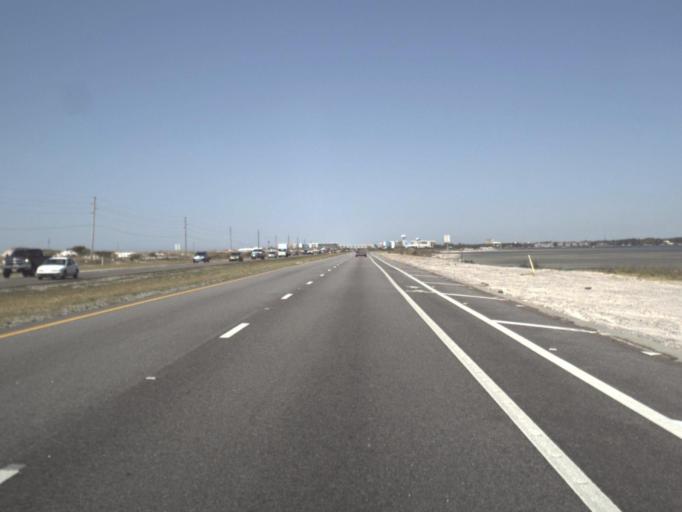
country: US
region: Florida
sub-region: Okaloosa County
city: Lake Lorraine
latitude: 30.3946
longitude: -86.5612
